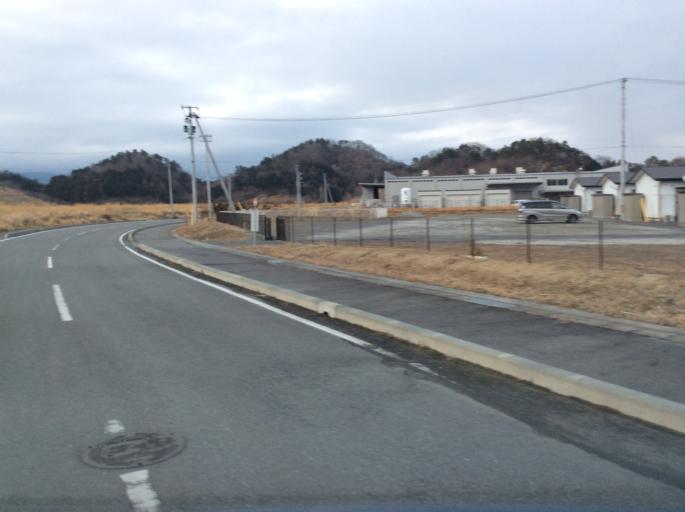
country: JP
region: Fukushima
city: Iwaki
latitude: 37.1244
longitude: 140.9653
